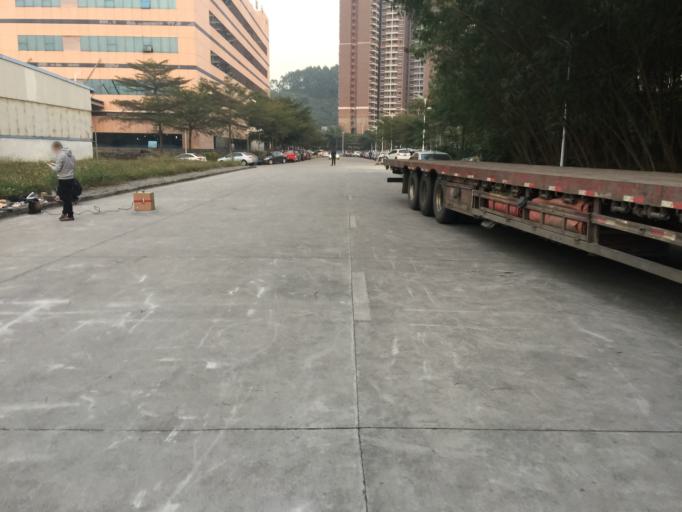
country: CN
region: Guangdong
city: Xin'an
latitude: 22.5798
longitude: 113.9262
